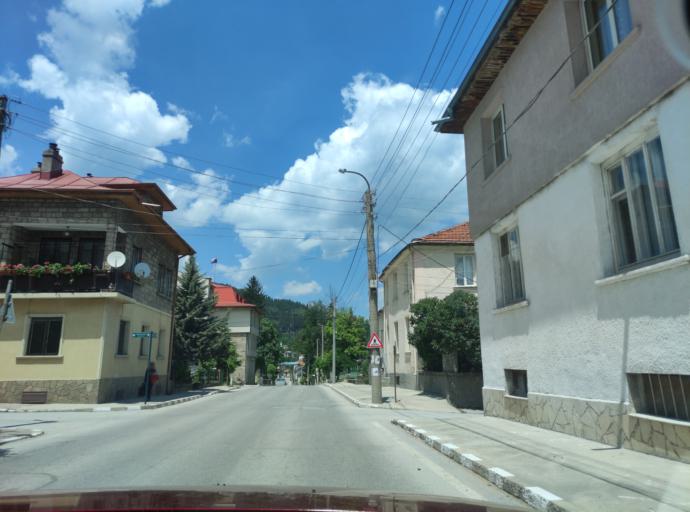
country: BG
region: Smolyan
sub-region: Obshtina Chepelare
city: Chepelare
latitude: 41.7238
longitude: 24.6851
